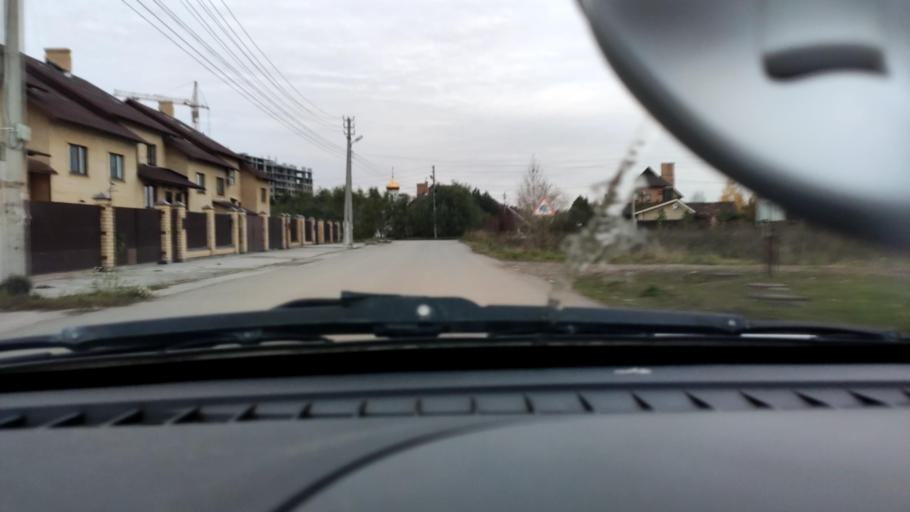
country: RU
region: Perm
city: Kondratovo
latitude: 57.9754
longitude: 56.1128
